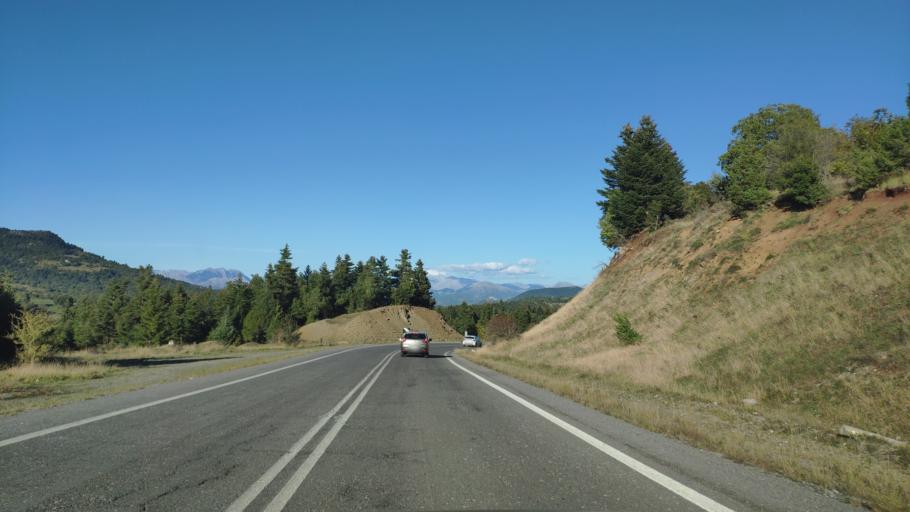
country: GR
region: Peloponnese
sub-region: Nomos Arkadias
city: Langadhia
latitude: 37.6571
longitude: 22.1381
